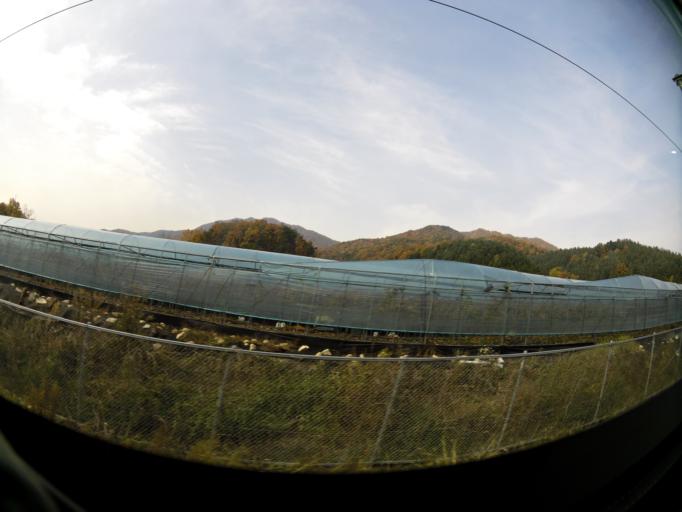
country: KR
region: Gyeongsangbuk-do
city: Gimcheon
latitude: 36.1767
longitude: 128.0068
